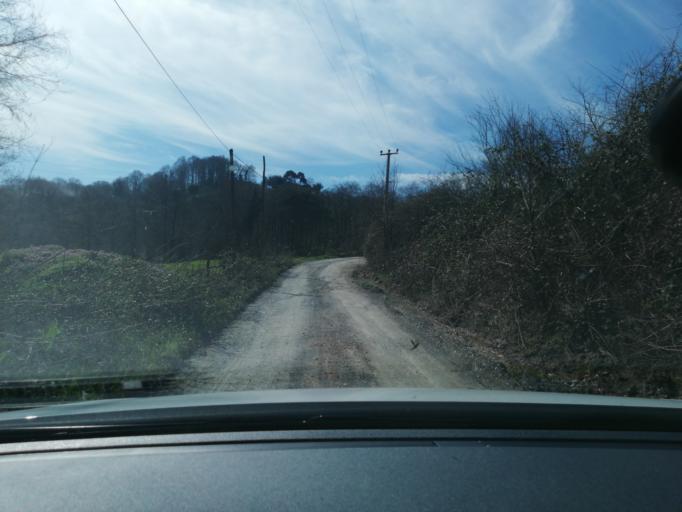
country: TR
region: Duzce
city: Akcakoca
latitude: 41.0890
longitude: 31.1974
